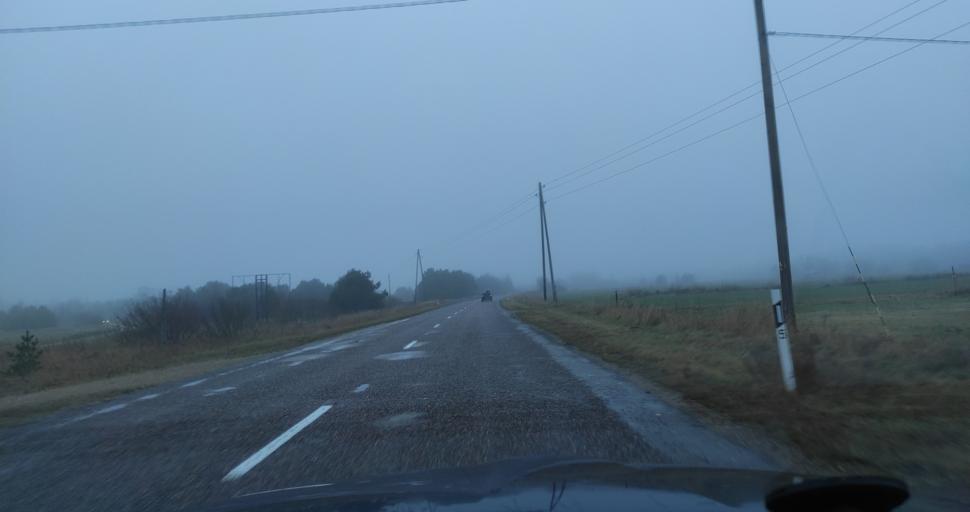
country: LV
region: Alsunga
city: Alsunga
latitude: 57.1196
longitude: 21.4247
